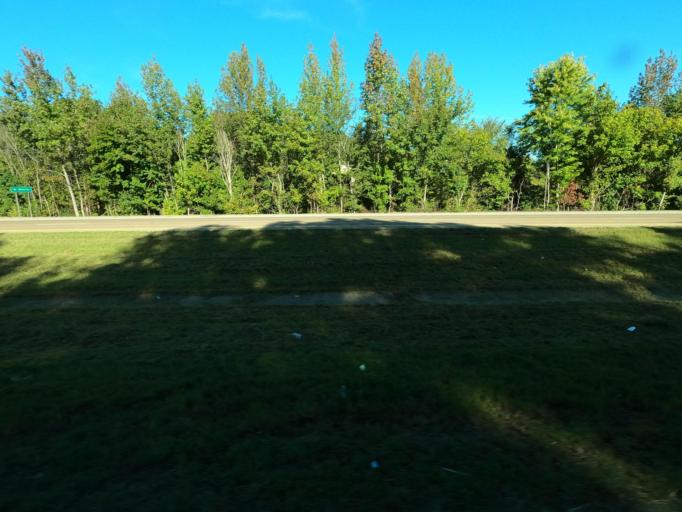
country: US
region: Tennessee
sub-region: Tipton County
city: Brighton
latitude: 35.4907
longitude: -89.7294
